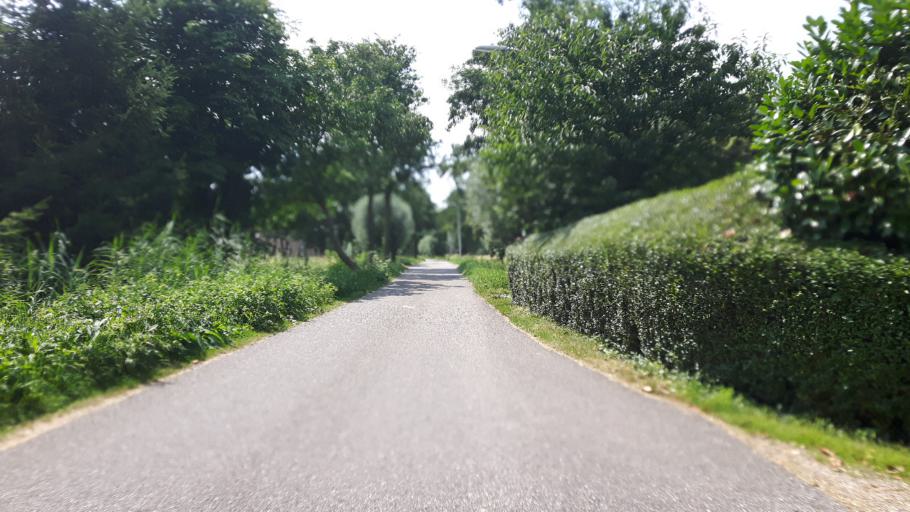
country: NL
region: South Holland
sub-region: Gemeente Giessenlanden
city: Giessenburg
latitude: 51.9100
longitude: 4.9119
